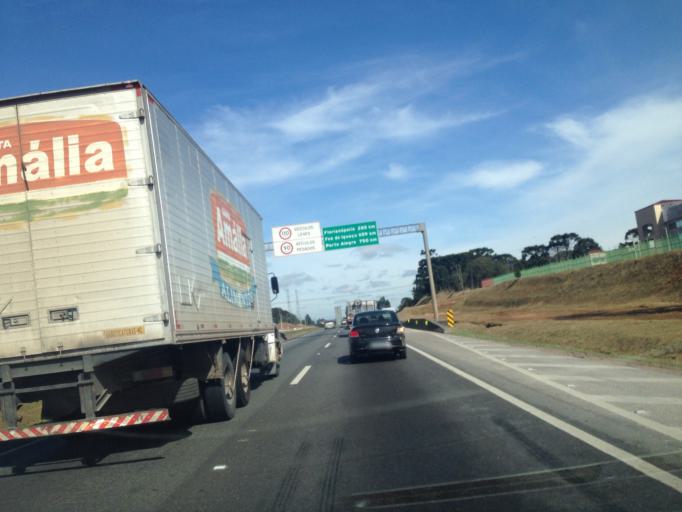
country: BR
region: Parana
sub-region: Sao Jose Dos Pinhais
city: Sao Jose dos Pinhais
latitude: -25.5158
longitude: -49.1313
